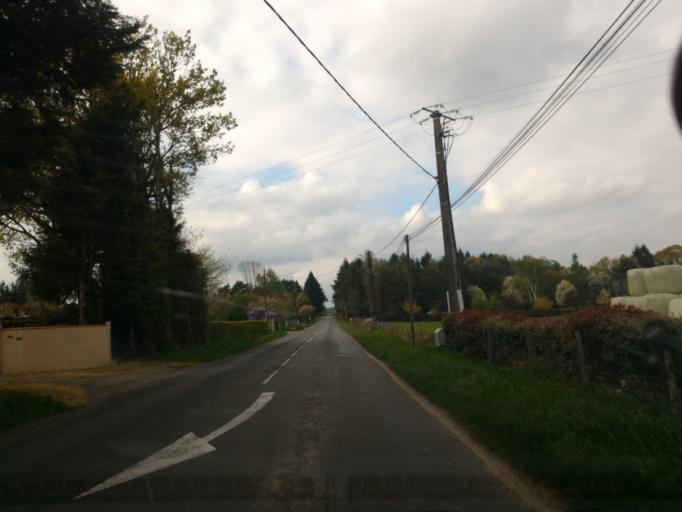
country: FR
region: Limousin
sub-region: Departement de la Haute-Vienne
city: Saint-Junien
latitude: 45.9158
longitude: 0.8926
